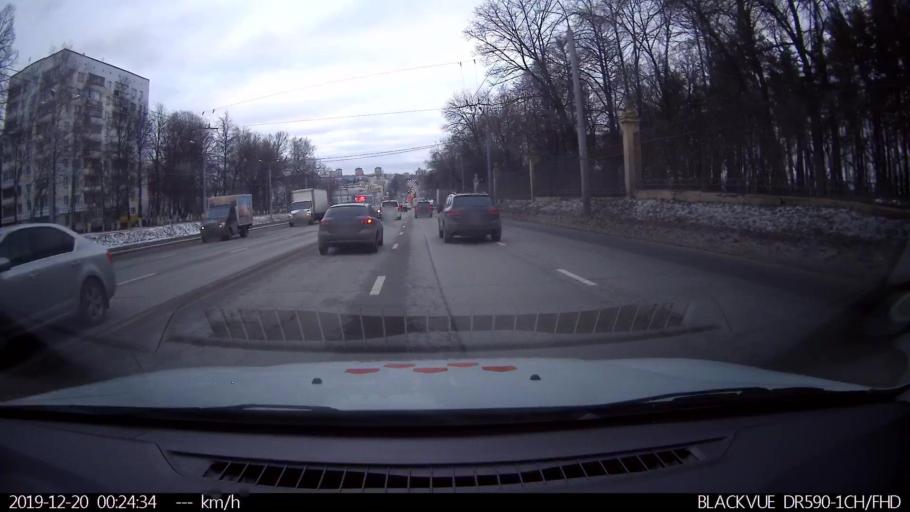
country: RU
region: Vladimir
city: Yur'yev-Pol'skiy
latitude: 56.6744
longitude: 39.5325
